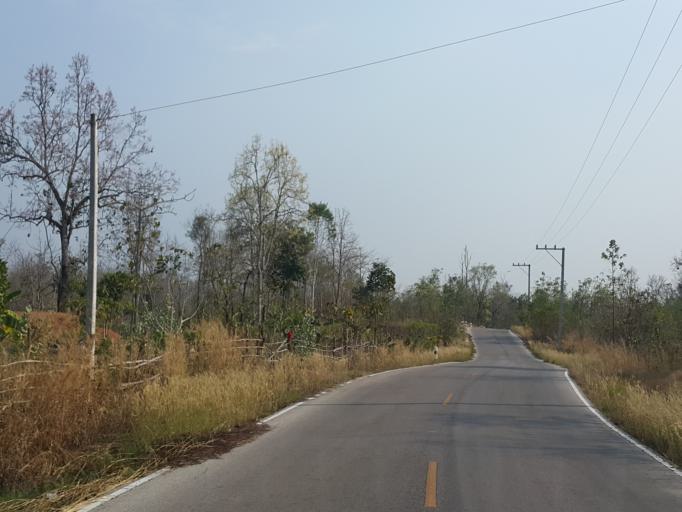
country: TH
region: Lampang
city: Chae Hom
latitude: 18.7353
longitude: 99.5464
